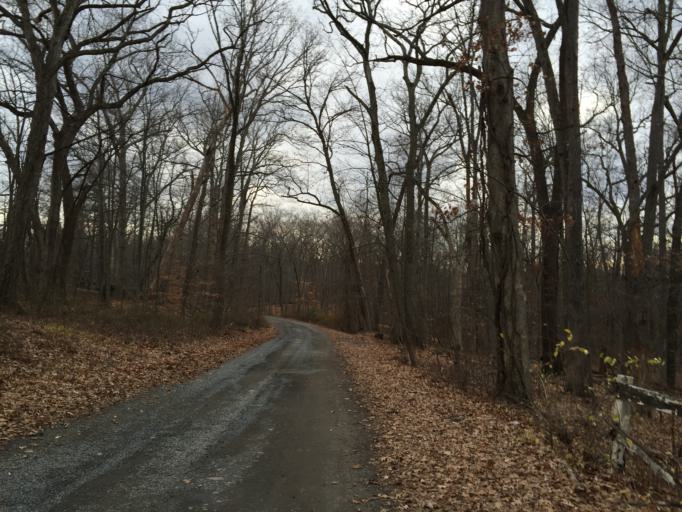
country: US
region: New Jersey
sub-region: Morris County
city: Chatham
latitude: 40.7225
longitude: -74.3897
